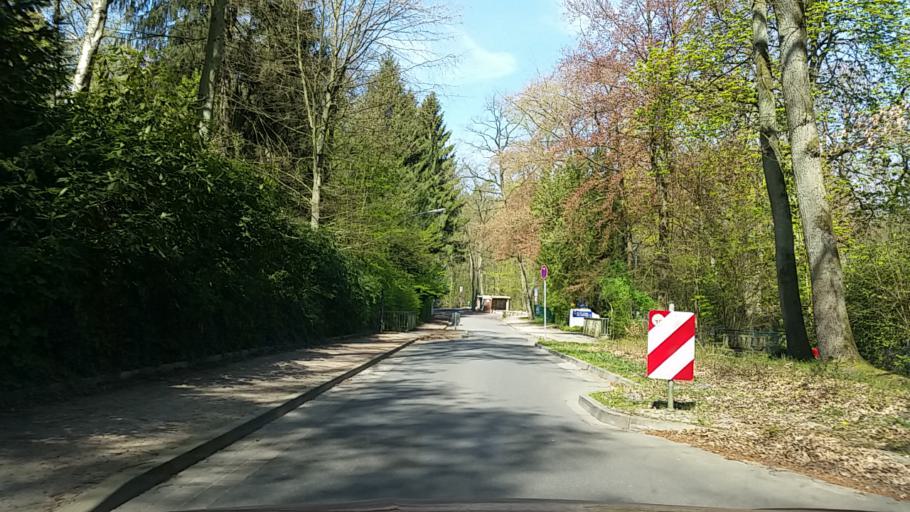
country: DE
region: Schleswig-Holstein
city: Wedel
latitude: 53.5890
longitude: 9.7526
